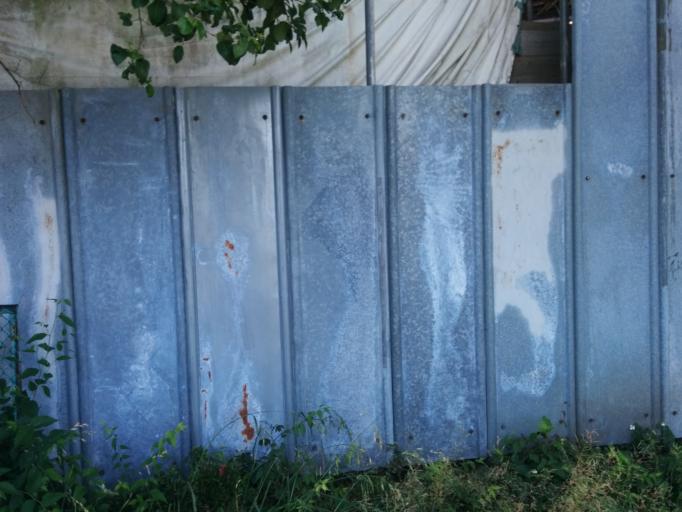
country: JP
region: Tokyo
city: Higashimurayama-shi
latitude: 35.7653
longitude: 139.4860
